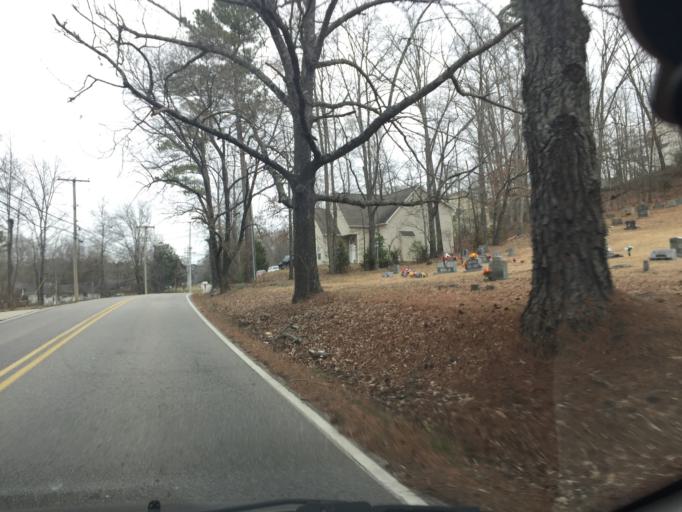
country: US
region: Tennessee
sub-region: Hamilton County
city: East Brainerd
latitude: 35.0145
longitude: -85.1265
